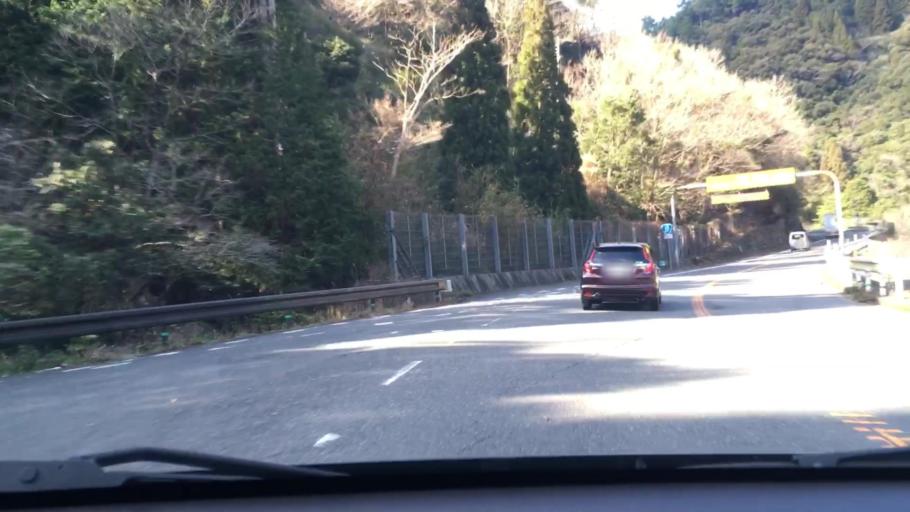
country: JP
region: Oita
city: Tsukumiura
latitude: 33.0008
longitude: 131.8040
